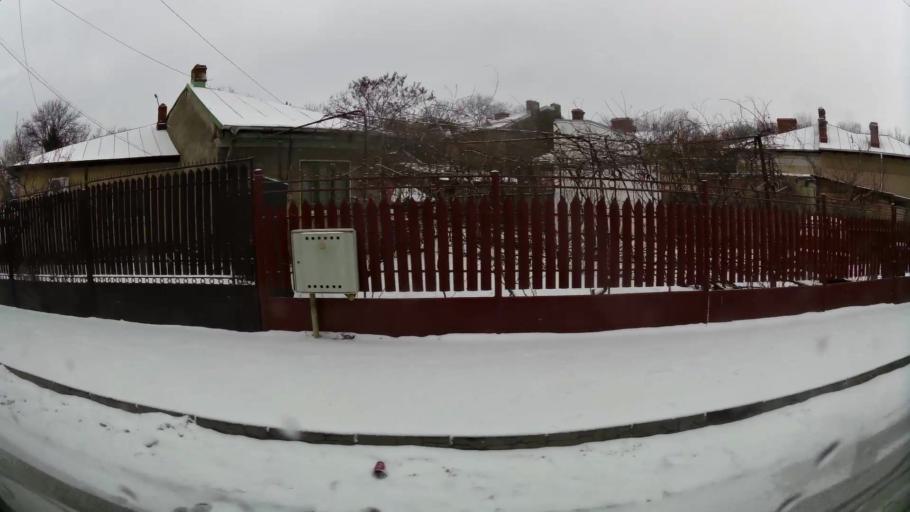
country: RO
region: Prahova
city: Ploiesti
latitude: 44.9320
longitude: 26.0157
